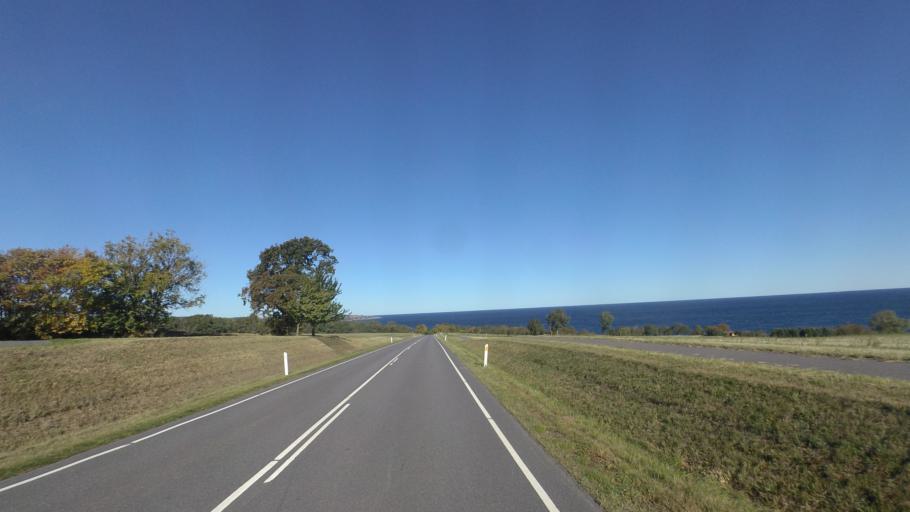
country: DK
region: Capital Region
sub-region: Bornholm Kommune
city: Akirkeby
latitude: 55.1696
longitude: 15.0282
